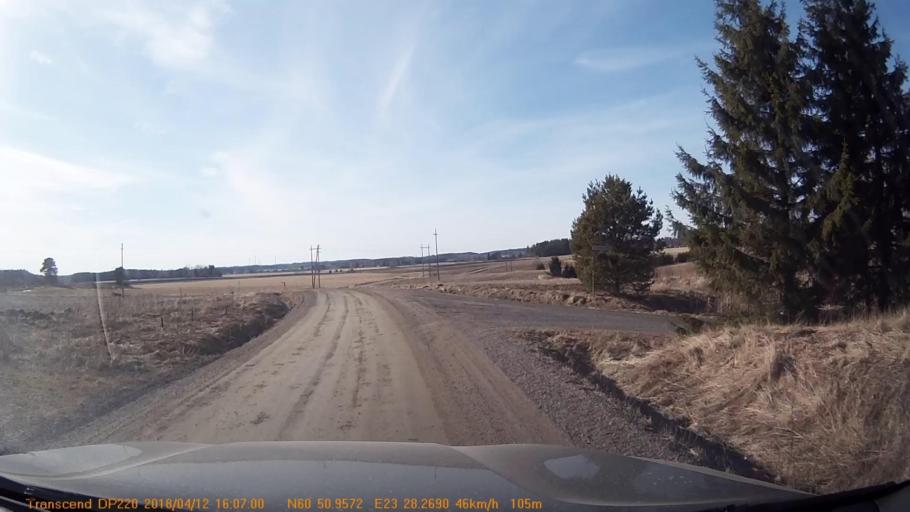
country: FI
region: Haeme
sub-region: Forssa
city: Jokioinen
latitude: 60.8494
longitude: 23.4709
